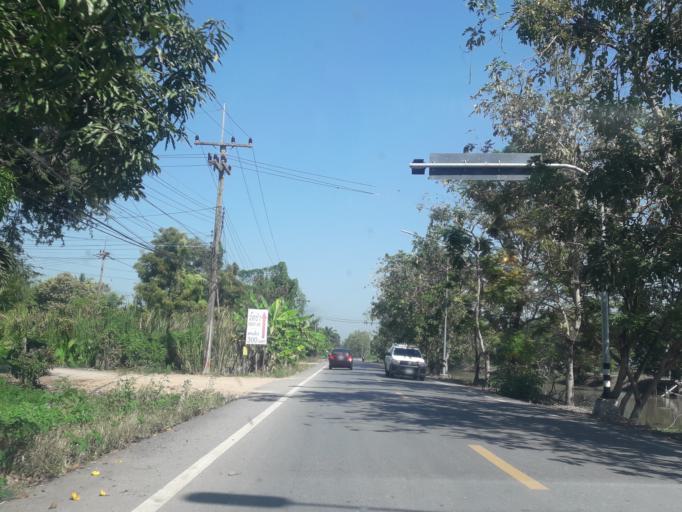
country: TH
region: Pathum Thani
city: Nong Suea
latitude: 14.1816
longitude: 100.8458
